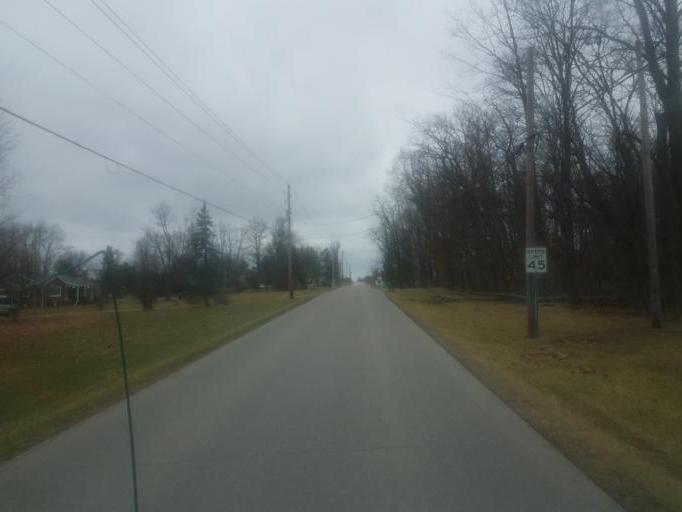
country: US
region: Ohio
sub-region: Crawford County
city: Galion
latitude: 40.7494
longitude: -82.8199
